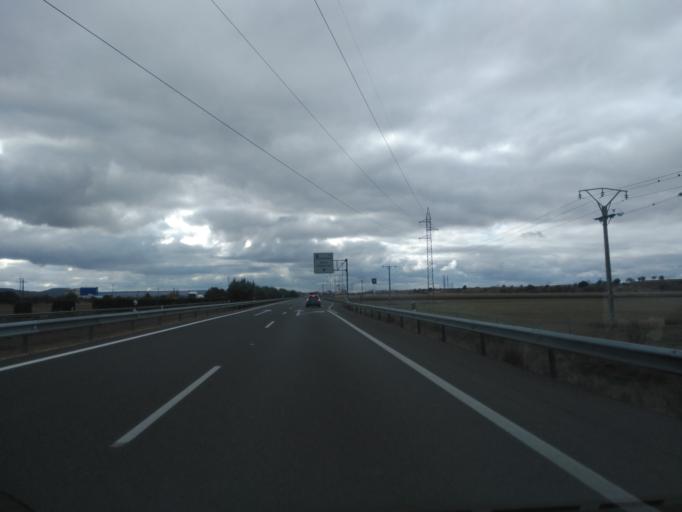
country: ES
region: Castille and Leon
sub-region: Provincia de Palencia
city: Duenas
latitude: 41.8444
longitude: -4.5622
